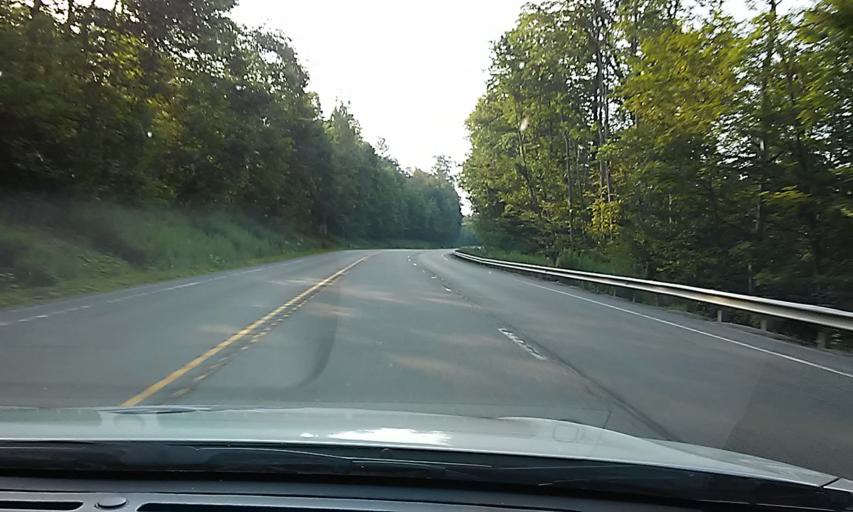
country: US
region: Pennsylvania
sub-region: McKean County
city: Smethport
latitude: 41.7144
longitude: -78.6021
